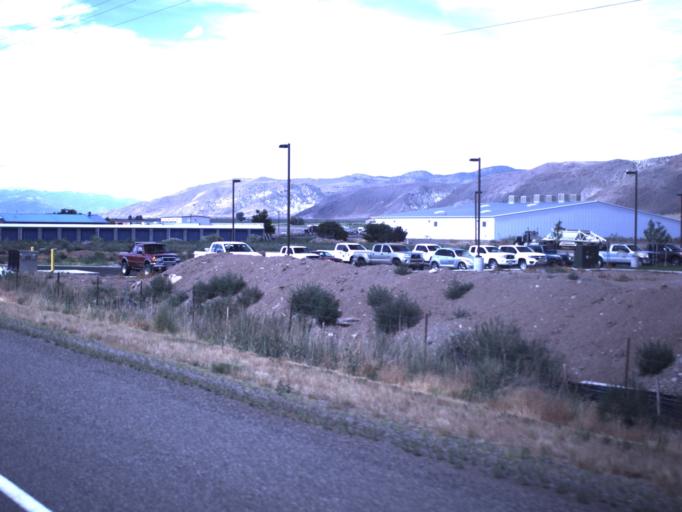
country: US
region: Utah
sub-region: Sevier County
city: Richfield
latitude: 38.7396
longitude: -112.0928
